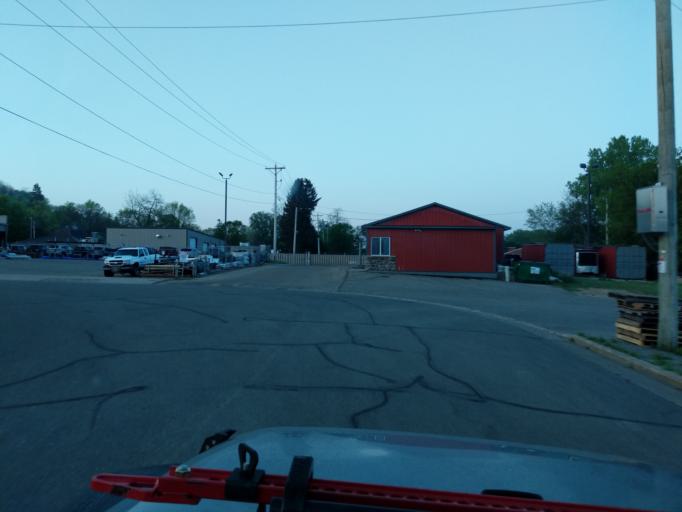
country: US
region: Wisconsin
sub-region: Pierce County
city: River Falls
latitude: 44.8673
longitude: -92.6231
